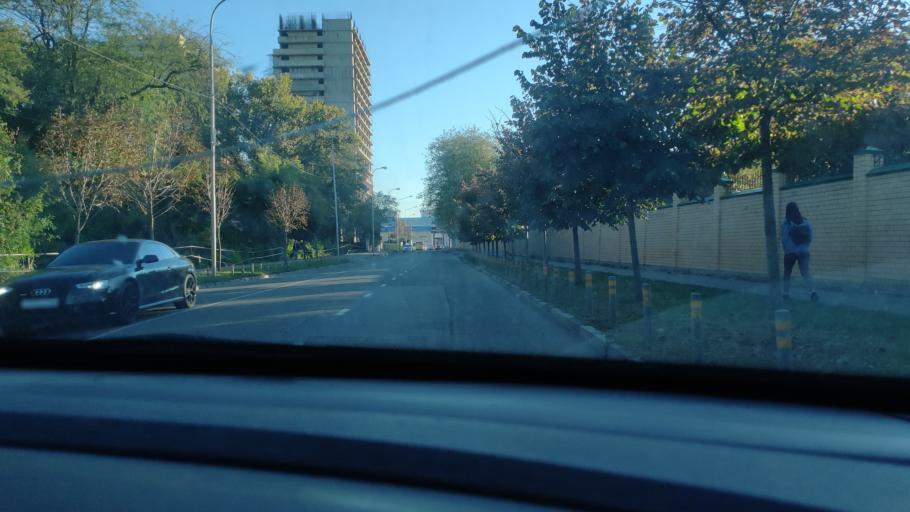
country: RU
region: Krasnodarskiy
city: Krasnodar
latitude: 45.0437
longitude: 38.9683
